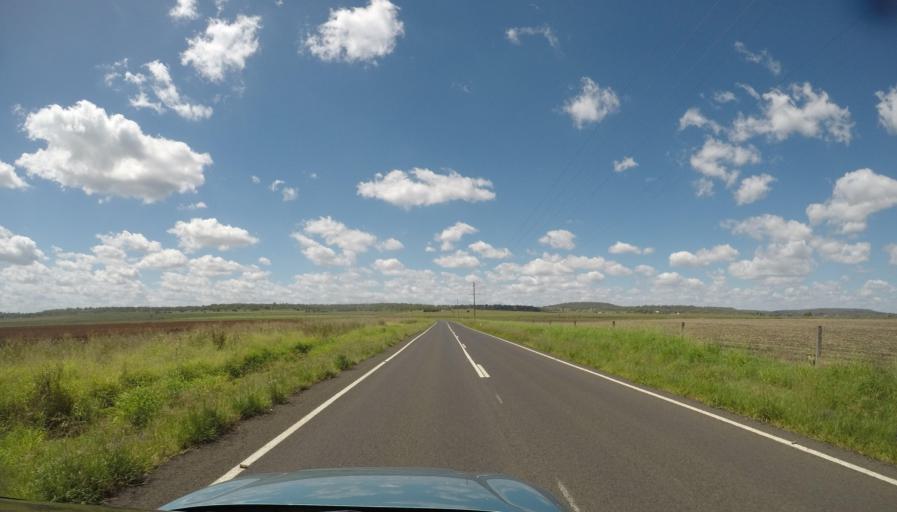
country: AU
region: Queensland
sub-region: Toowoomba
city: Oakey
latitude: -27.5412
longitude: 151.6476
